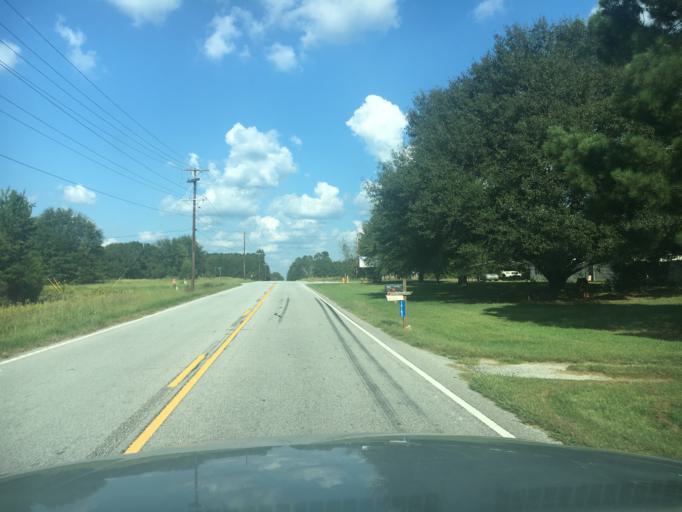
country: US
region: South Carolina
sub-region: Greenwood County
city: Ware Shoals
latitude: 34.5122
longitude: -82.2053
